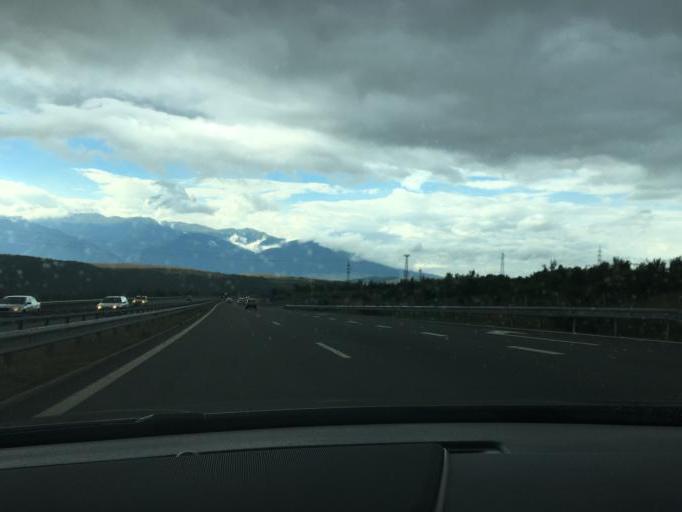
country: BG
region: Kyustendil
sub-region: Obshtina Dupnitsa
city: Dupnitsa
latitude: 42.3406
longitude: 23.0962
